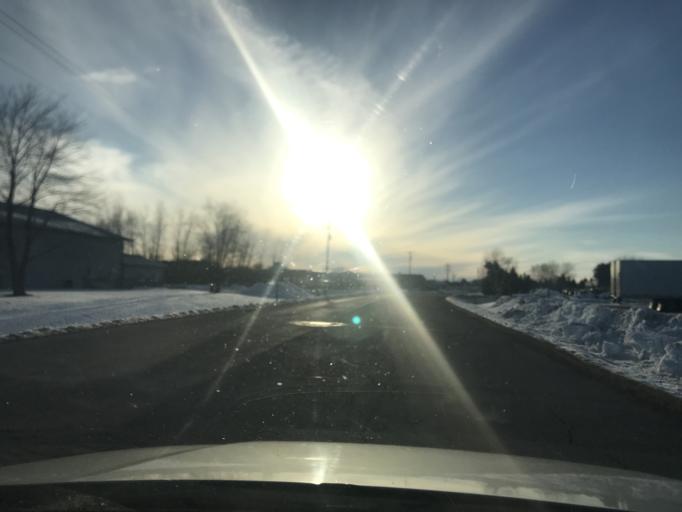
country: US
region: Wisconsin
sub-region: Marinette County
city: Peshtigo
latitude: 45.0559
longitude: -87.7267
